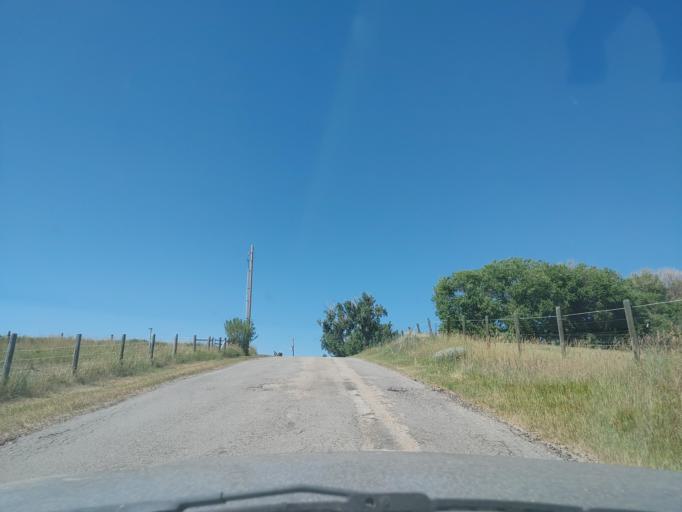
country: US
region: Montana
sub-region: Ravalli County
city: Hamilton
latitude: 46.3151
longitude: -114.0612
